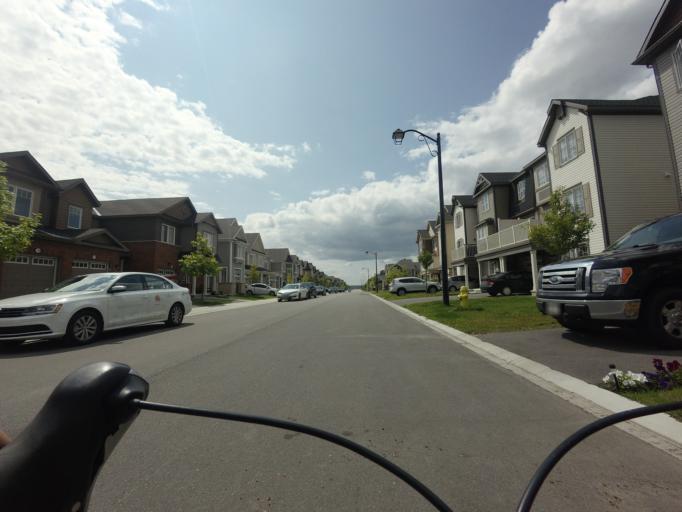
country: CA
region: Ontario
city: Bells Corners
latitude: 45.2785
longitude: -75.8368
